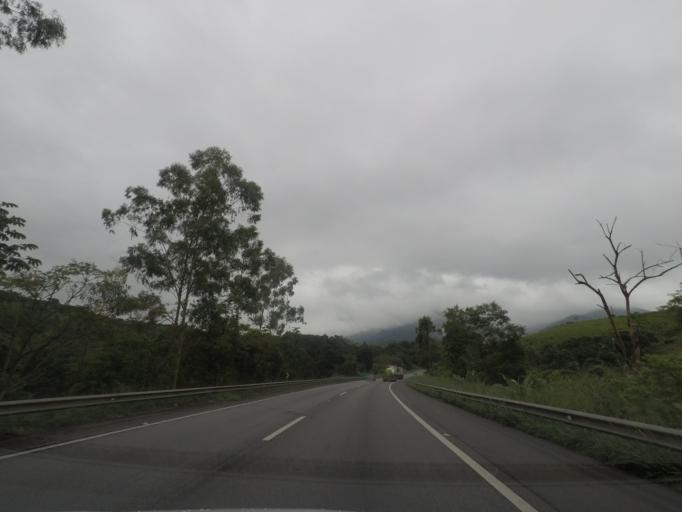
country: BR
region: Sao Paulo
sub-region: Cajati
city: Cajati
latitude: -24.7788
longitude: -48.1985
